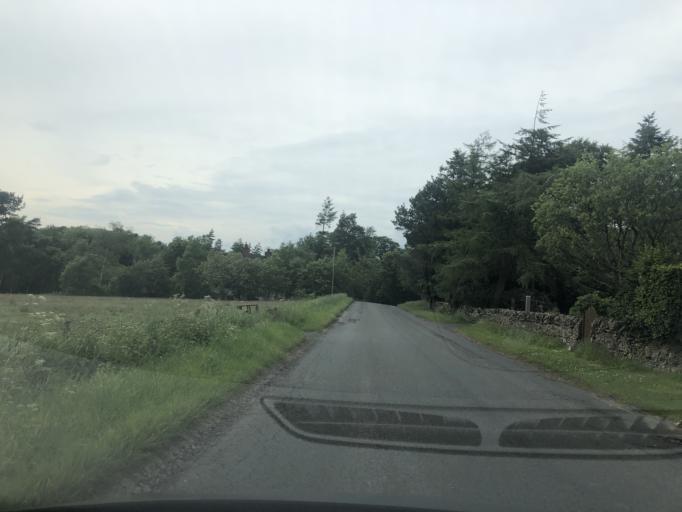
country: GB
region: Scotland
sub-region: The Scottish Borders
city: West Linton
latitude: 55.7414
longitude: -3.3395
